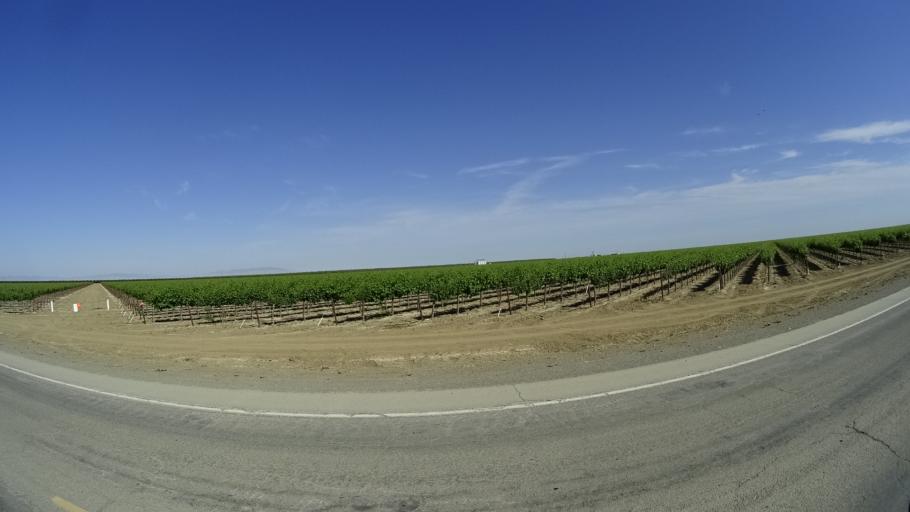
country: US
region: California
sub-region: Fresno County
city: Huron
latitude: 36.1560
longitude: -119.9881
